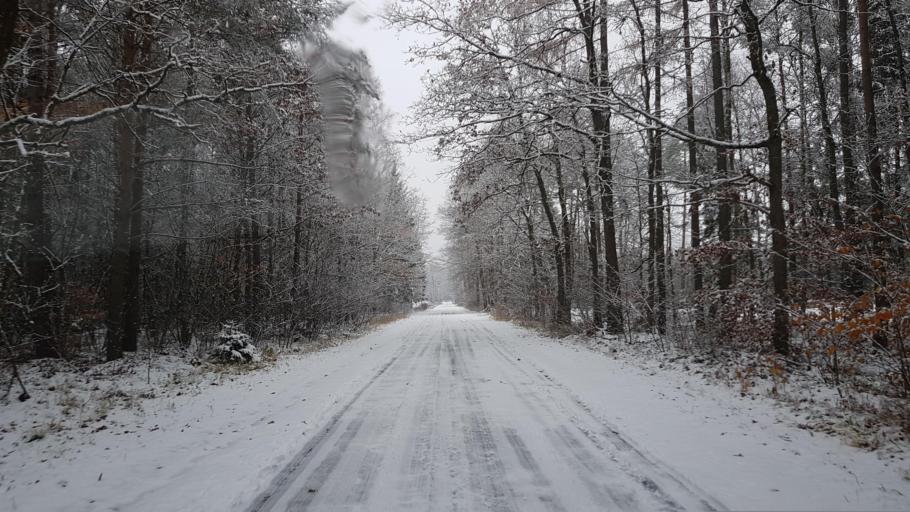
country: PL
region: West Pomeranian Voivodeship
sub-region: Powiat lobeski
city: Resko
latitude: 53.7860
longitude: 15.5321
